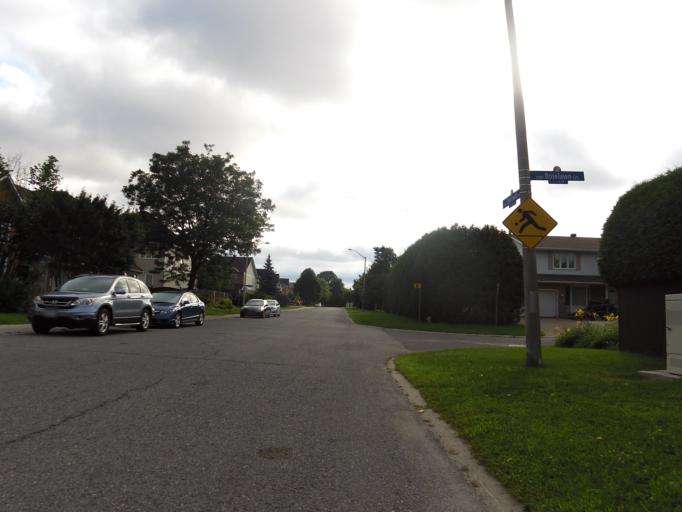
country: CA
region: Ontario
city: Bells Corners
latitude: 45.3326
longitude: -75.7679
